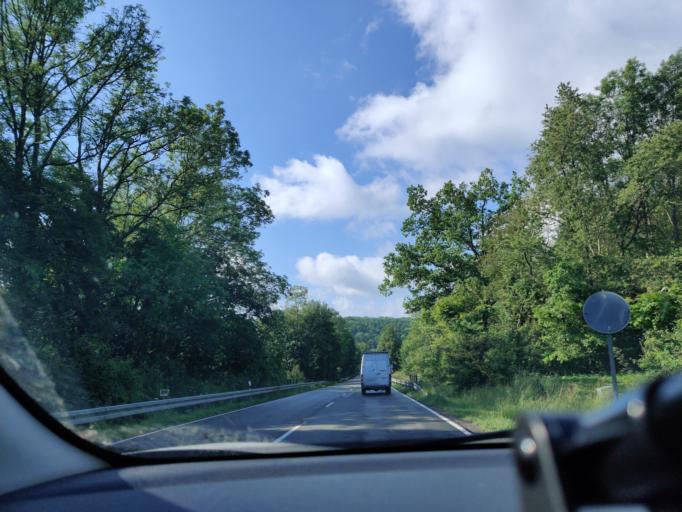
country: FR
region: Lorraine
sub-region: Departement de la Moselle
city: Bliesbruck
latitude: 49.1479
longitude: 7.1525
